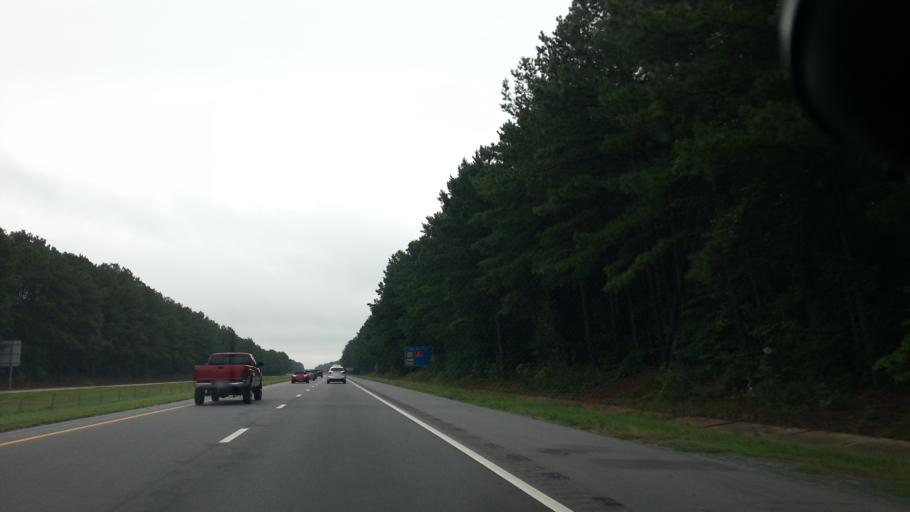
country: US
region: North Carolina
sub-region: Cumberland County
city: Fort Bragg
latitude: 35.0861
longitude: -78.9656
